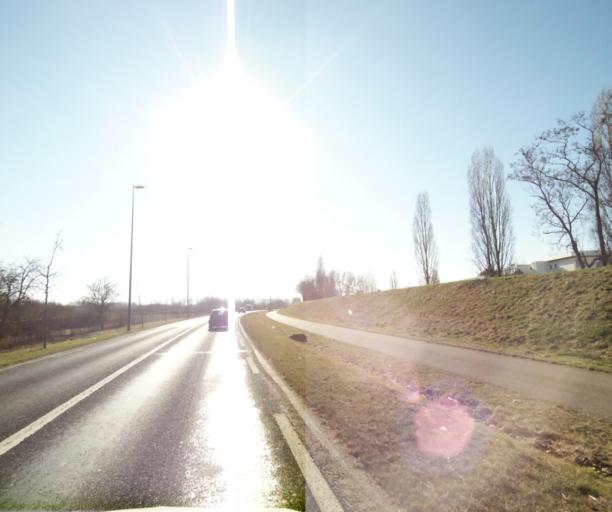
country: FR
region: Lorraine
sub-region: Departement de Meurthe-et-Moselle
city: Essey-les-Nancy
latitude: 48.6967
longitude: 6.2201
